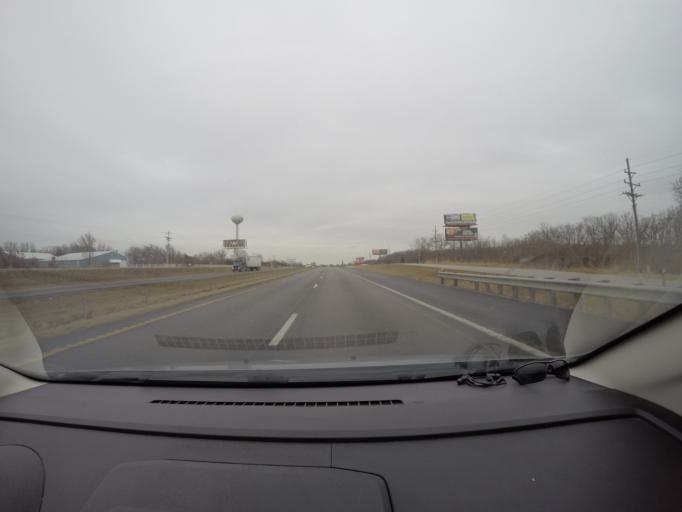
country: US
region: Missouri
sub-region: Warren County
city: Warrenton
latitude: 38.8262
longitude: -91.2057
